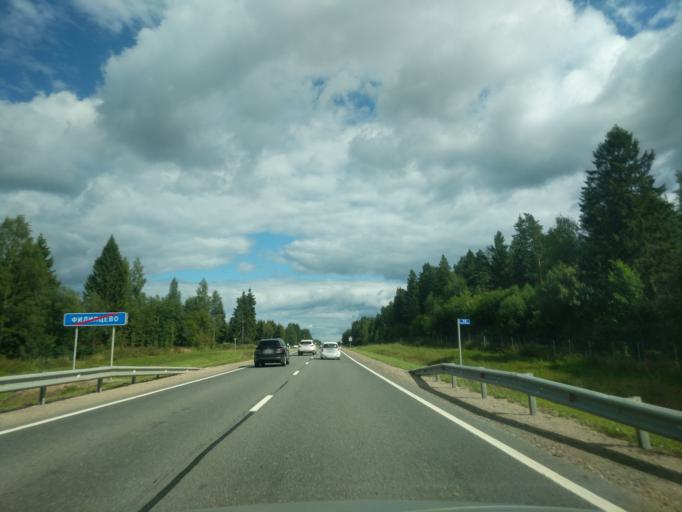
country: RU
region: Kostroma
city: Oktyabr'skiy
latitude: 57.7981
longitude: 41.2308
